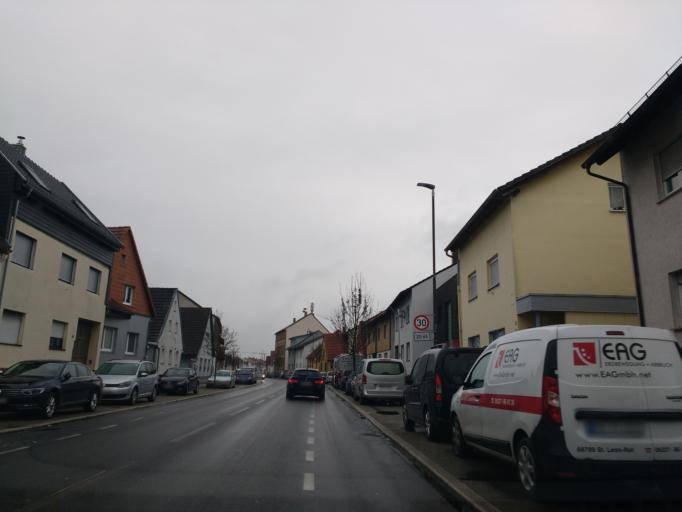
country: DE
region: Baden-Wuerttemberg
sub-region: Karlsruhe Region
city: Hambrucken
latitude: 49.1840
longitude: 8.5459
